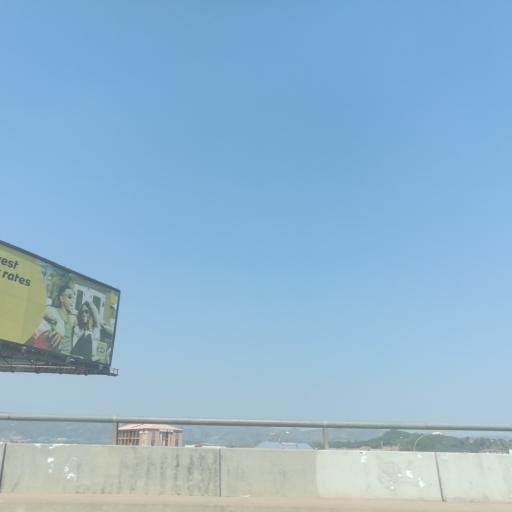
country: NG
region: Abuja Federal Capital Territory
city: Abuja
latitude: 9.0781
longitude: 7.4563
